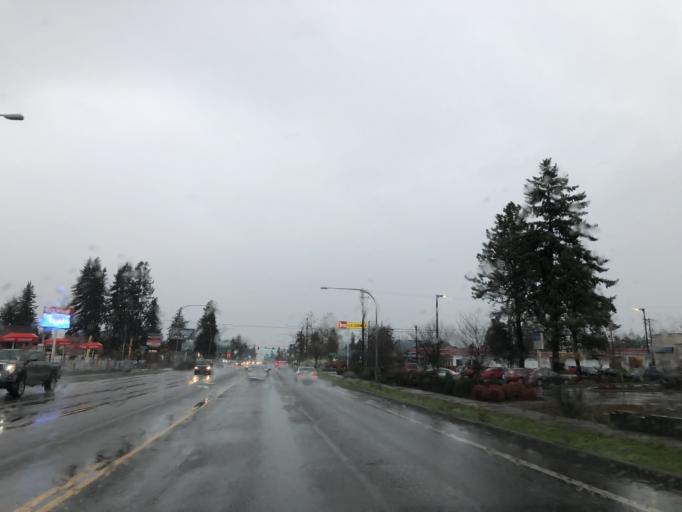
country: US
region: Washington
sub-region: Pierce County
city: Spanaway
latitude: 47.1024
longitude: -122.4348
